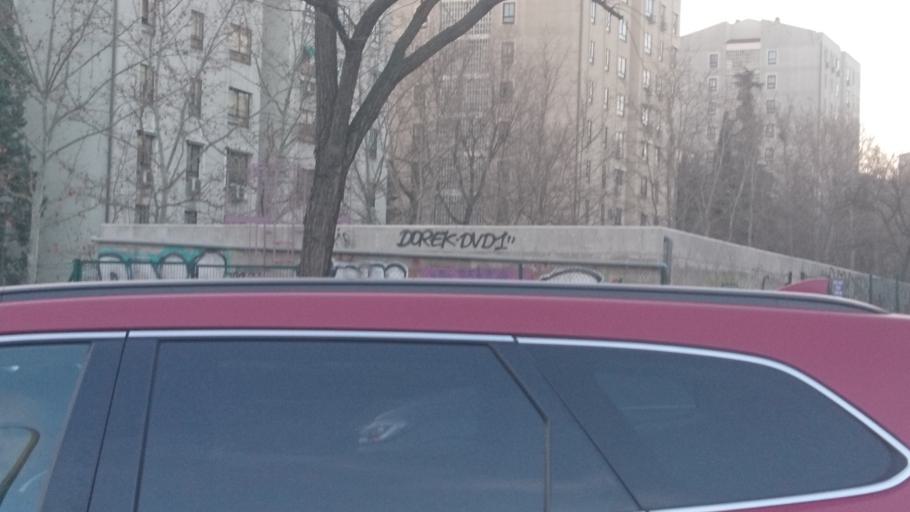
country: ES
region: Madrid
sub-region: Provincia de Madrid
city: Usera
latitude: 40.3730
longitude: -3.7120
